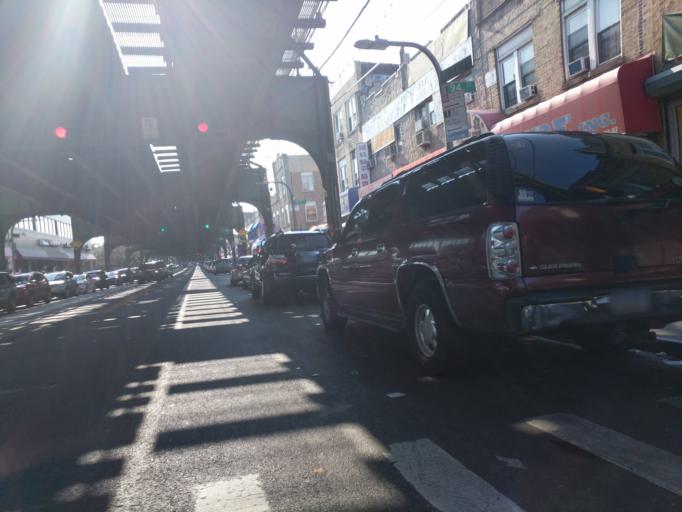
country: US
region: New York
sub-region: Queens County
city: Borough of Queens
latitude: 40.7489
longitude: -73.8722
